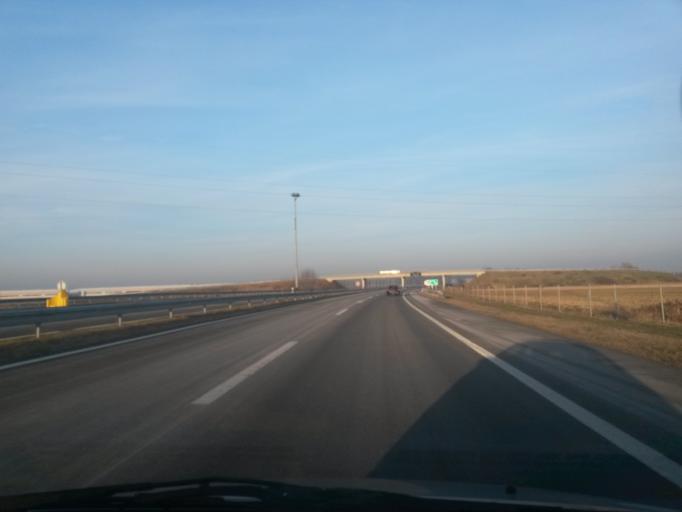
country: HR
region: Medimurska
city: Kursanec
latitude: 46.2621
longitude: 16.4014
